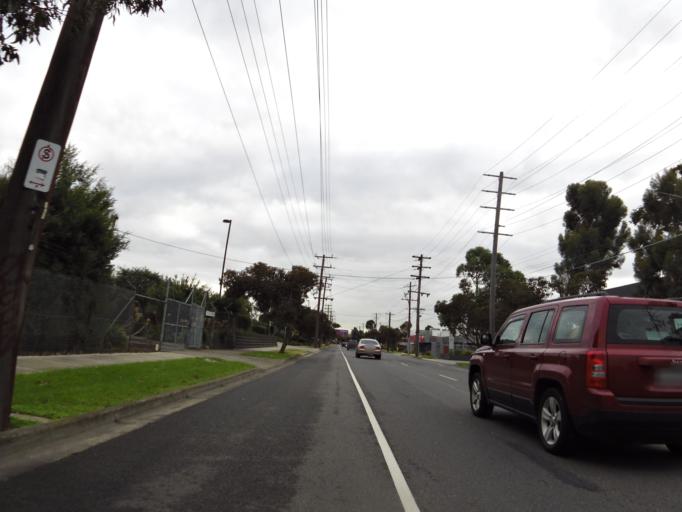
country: AU
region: Victoria
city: Heidelberg West
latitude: -37.7463
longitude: 145.0300
